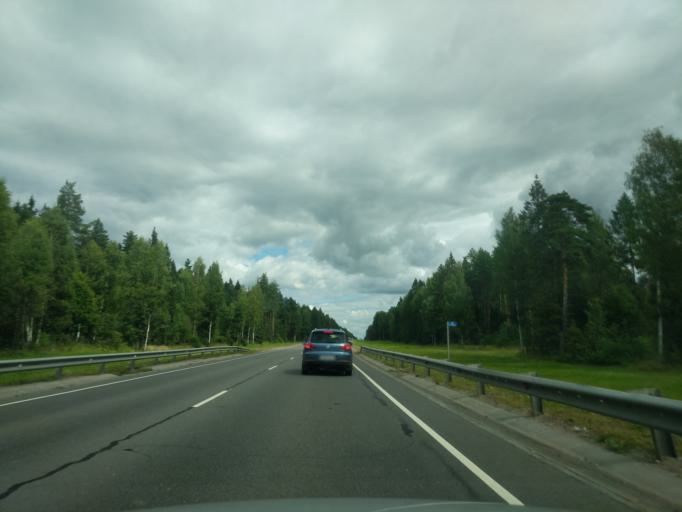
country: RU
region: Jaroslavl
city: Nekrasovskoye
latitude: 57.5989
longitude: 40.3134
